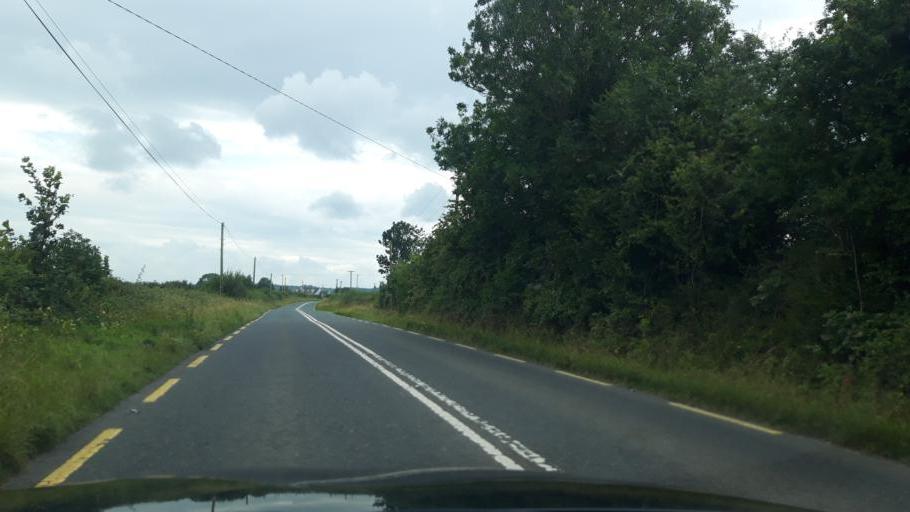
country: IE
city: Ballylinan
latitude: 52.9266
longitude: -7.0615
